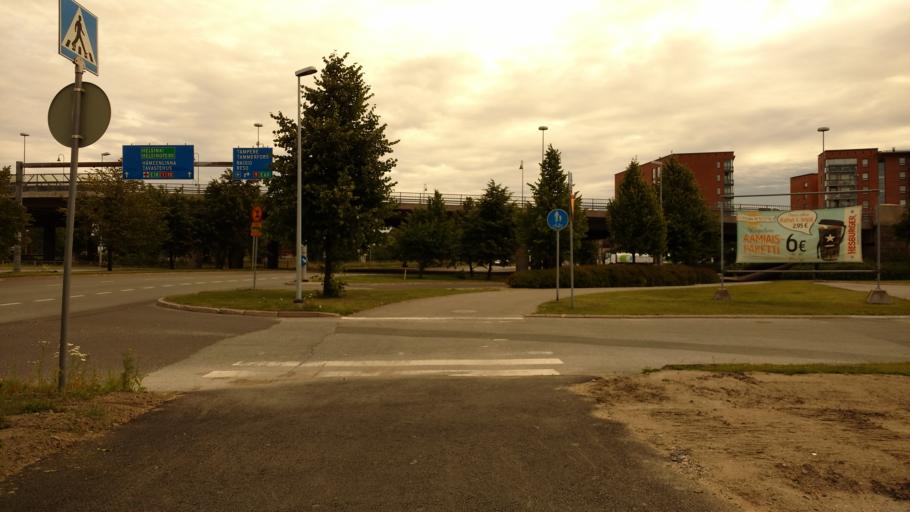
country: FI
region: Varsinais-Suomi
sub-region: Turku
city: Turku
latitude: 60.4580
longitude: 22.2672
